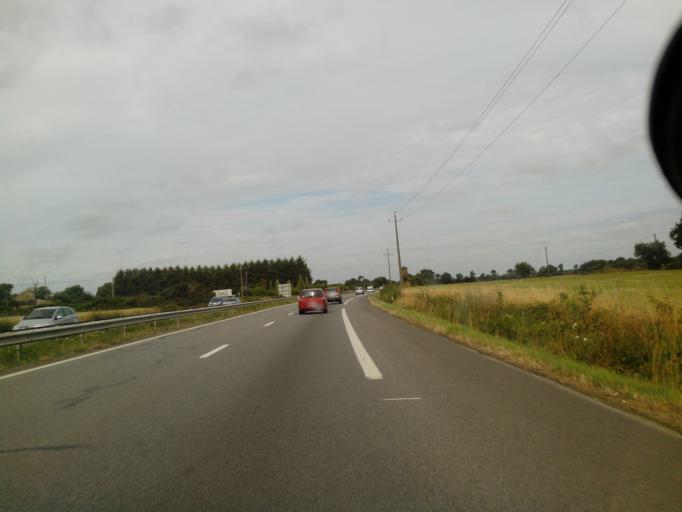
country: FR
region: Brittany
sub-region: Departement du Morbihan
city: Peaule
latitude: 47.5367
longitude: -2.4076
